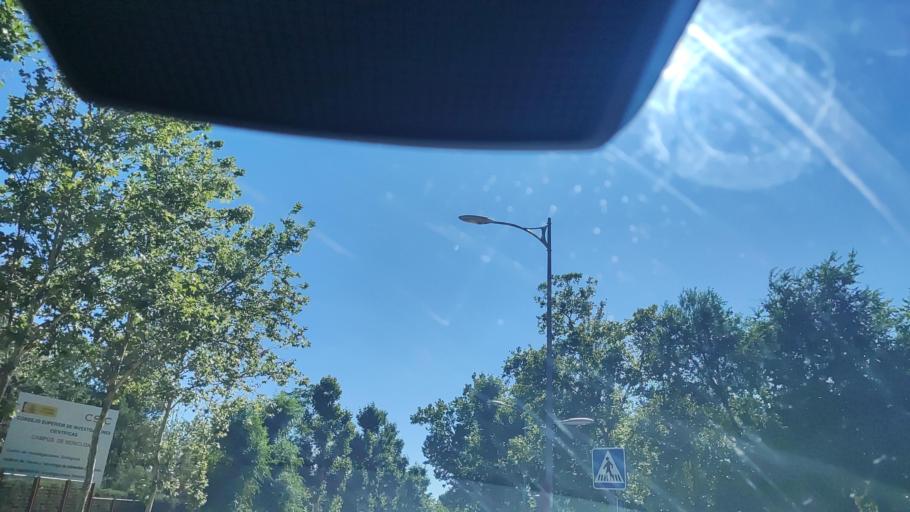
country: ES
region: Madrid
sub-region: Provincia de Madrid
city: Moncloa-Aravaca
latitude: 40.4489
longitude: -3.7212
